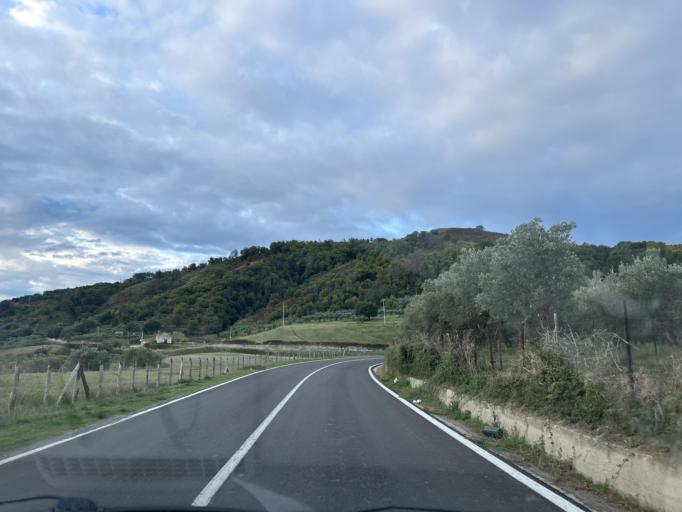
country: IT
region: Calabria
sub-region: Provincia di Catanzaro
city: Montauro
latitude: 38.7581
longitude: 16.5075
